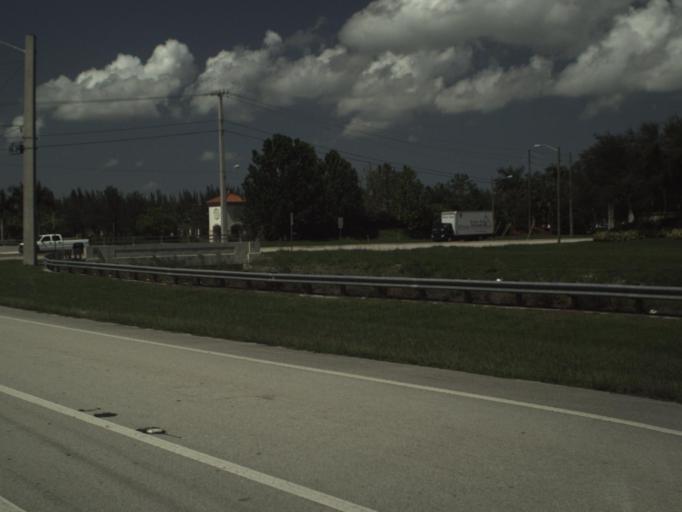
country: US
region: Florida
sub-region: Palm Beach County
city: Wellington
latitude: 26.5907
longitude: -80.2057
